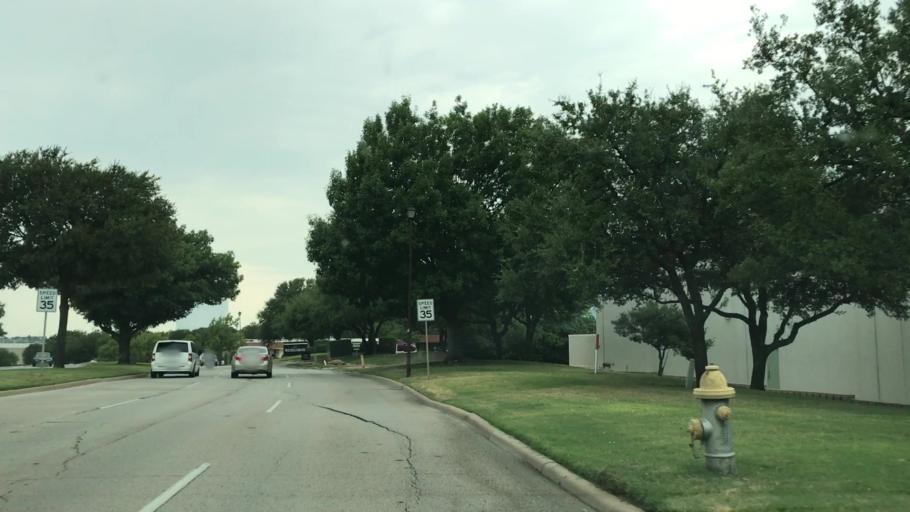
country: US
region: Texas
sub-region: Dallas County
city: Irving
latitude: 32.8851
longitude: -96.9716
